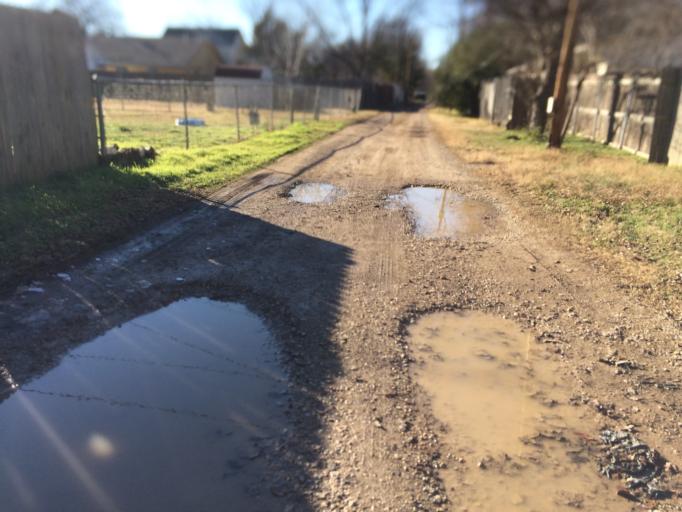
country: US
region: Oklahoma
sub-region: Cleveland County
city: Norman
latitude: 35.2301
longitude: -97.4465
